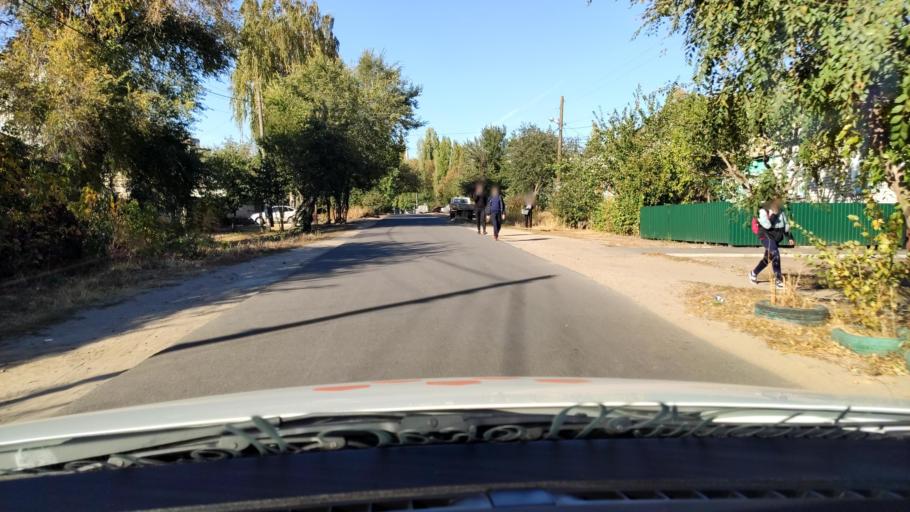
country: RU
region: Voronezj
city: Voronezh
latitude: 51.7003
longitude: 39.1685
